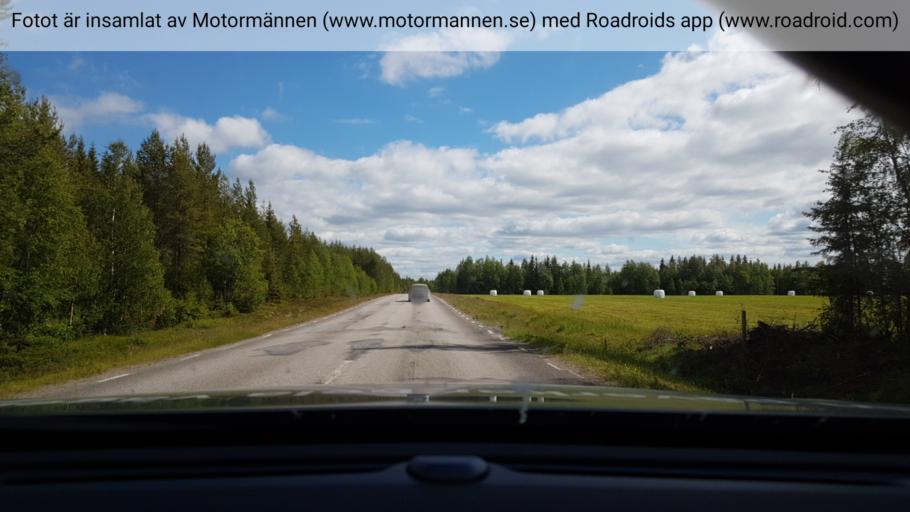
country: SE
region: Vaesterbotten
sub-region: Sorsele Kommun
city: Sorsele
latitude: 65.5958
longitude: 17.5013
